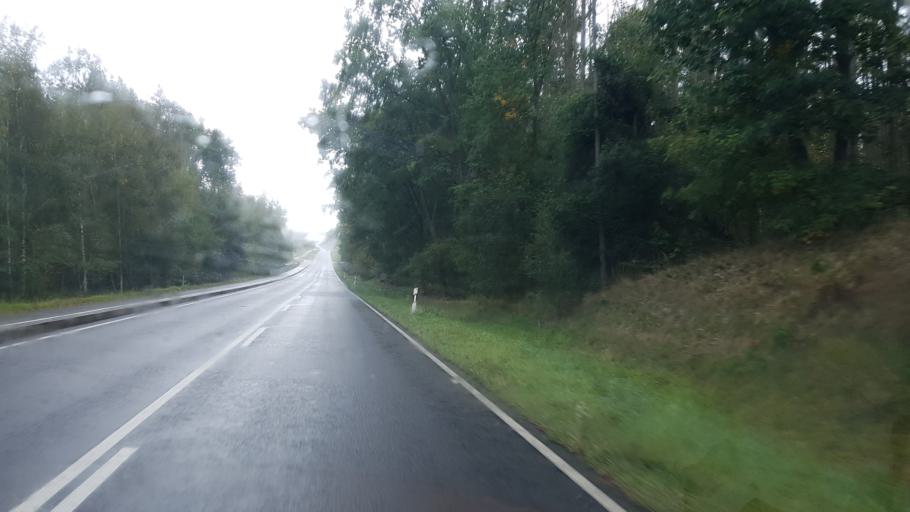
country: DE
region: Saxony
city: Dahlen
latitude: 51.3795
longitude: 12.9924
